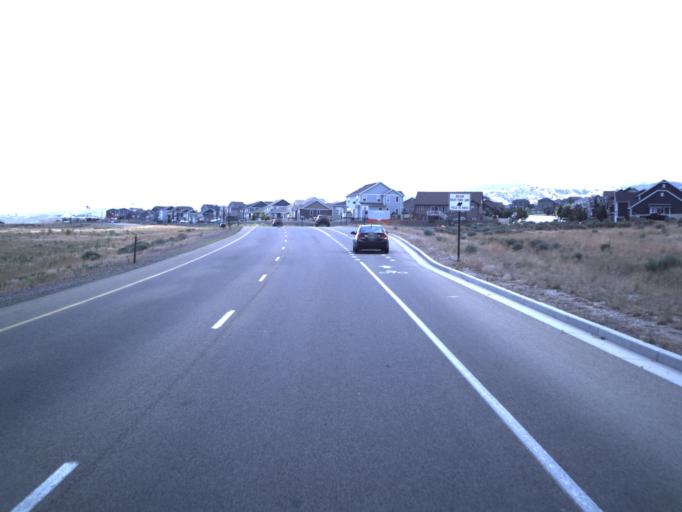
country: US
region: Utah
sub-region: Salt Lake County
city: Herriman
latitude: 40.4946
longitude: -112.0046
